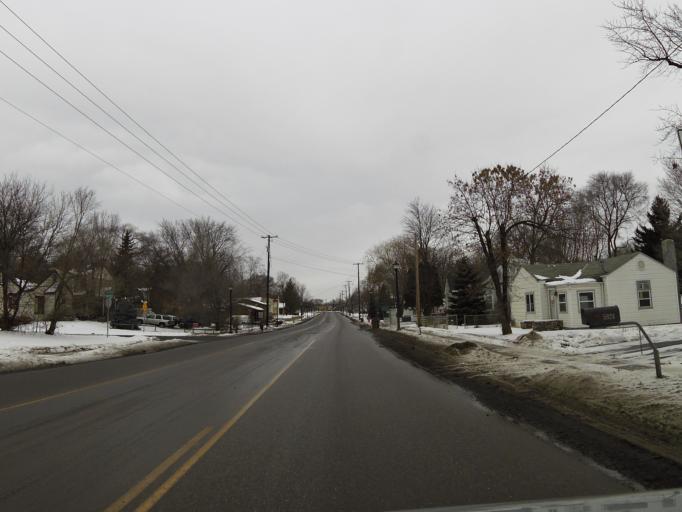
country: US
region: Minnesota
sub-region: Washington County
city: Newport
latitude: 44.8633
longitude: -93.0228
